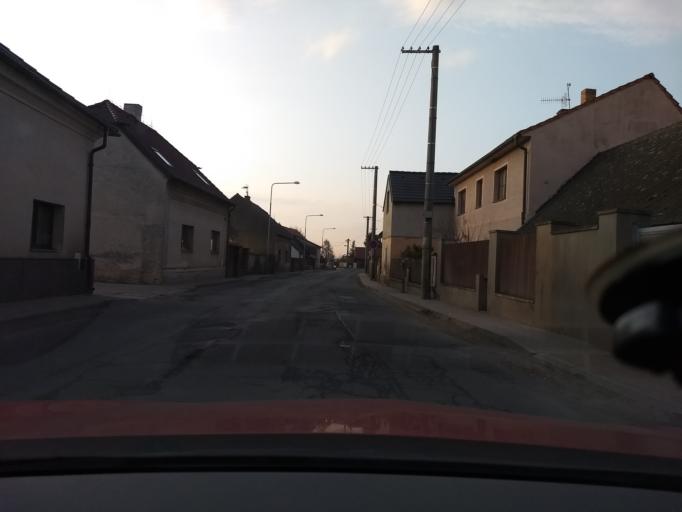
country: CZ
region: Central Bohemia
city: Rudna
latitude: 50.0410
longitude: 14.1873
